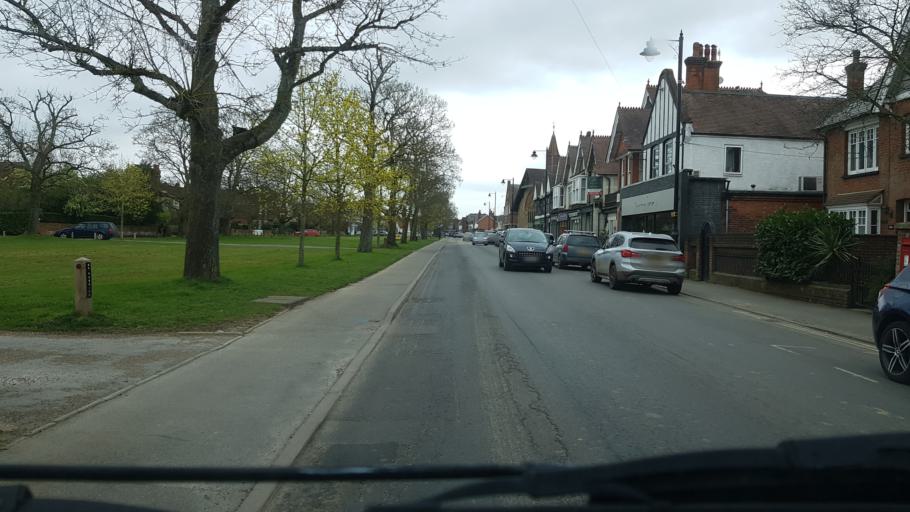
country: GB
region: England
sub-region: Surrey
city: Cranleigh
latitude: 51.1427
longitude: -0.4942
